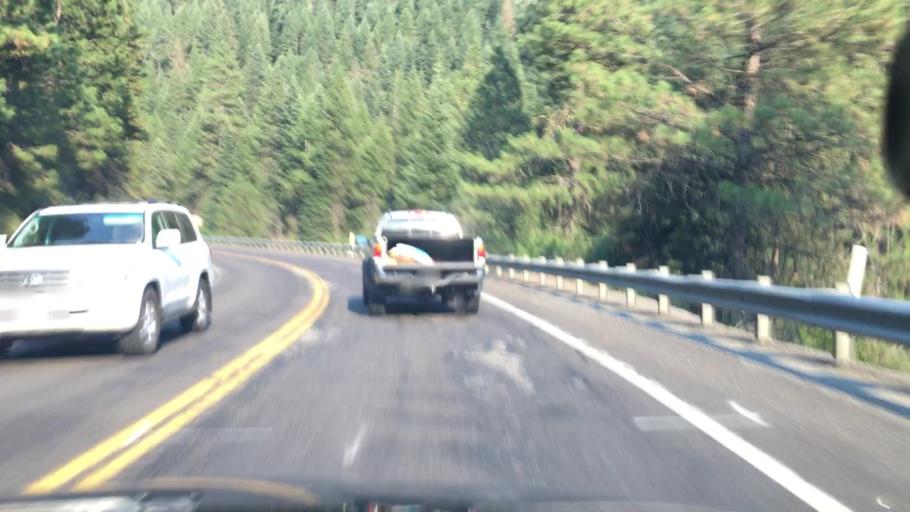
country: US
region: Idaho
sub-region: Valley County
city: Cascade
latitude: 44.2444
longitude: -116.0998
